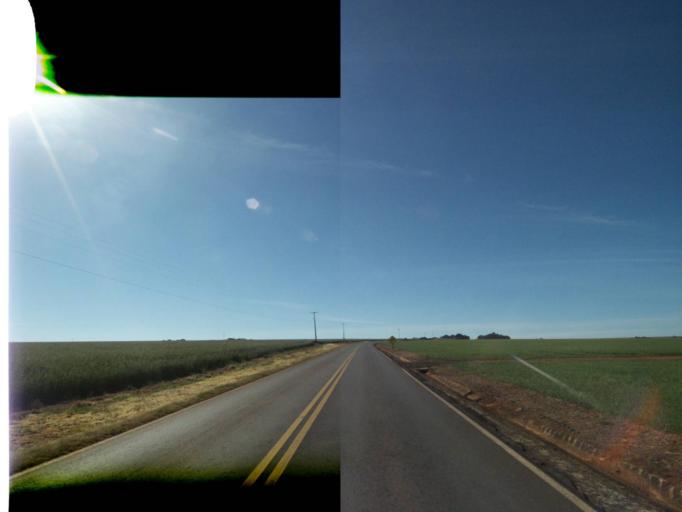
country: BR
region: Parana
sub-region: Tibagi
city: Tibagi
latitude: -24.5198
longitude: -50.3364
